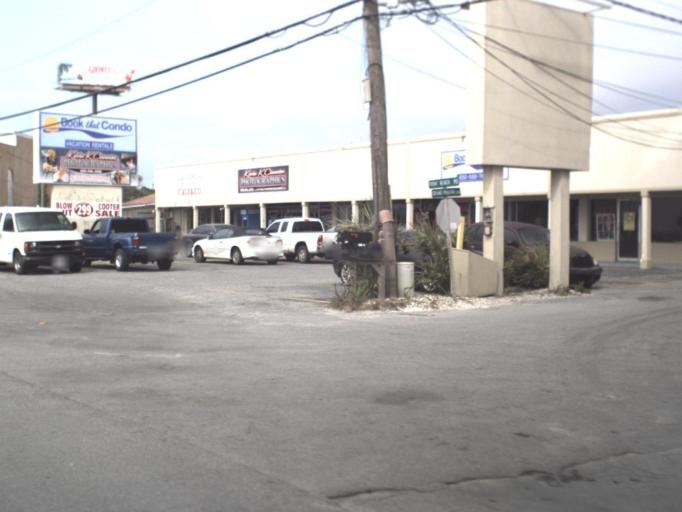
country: US
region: Florida
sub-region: Bay County
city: Panama City Beach
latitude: 30.1876
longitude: -85.8256
